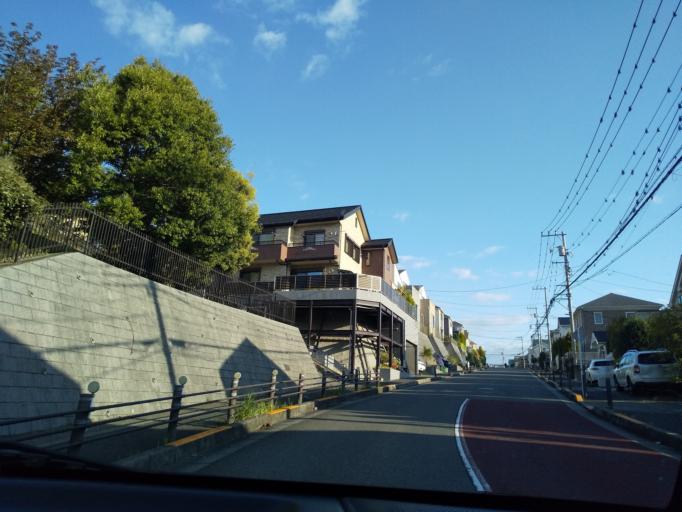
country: JP
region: Tokyo
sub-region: Machida-shi
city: Machida
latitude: 35.5839
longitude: 139.4562
